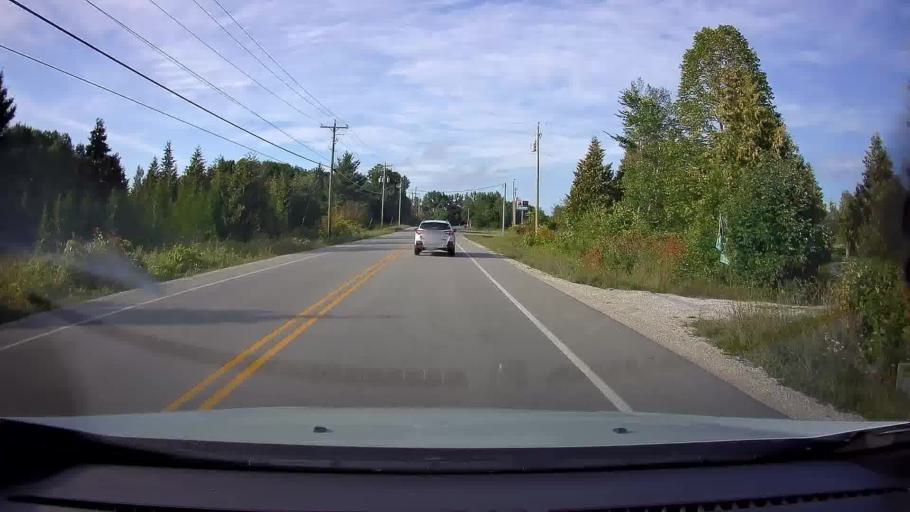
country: US
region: Wisconsin
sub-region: Door County
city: Sturgeon Bay
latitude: 45.1681
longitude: -87.1325
